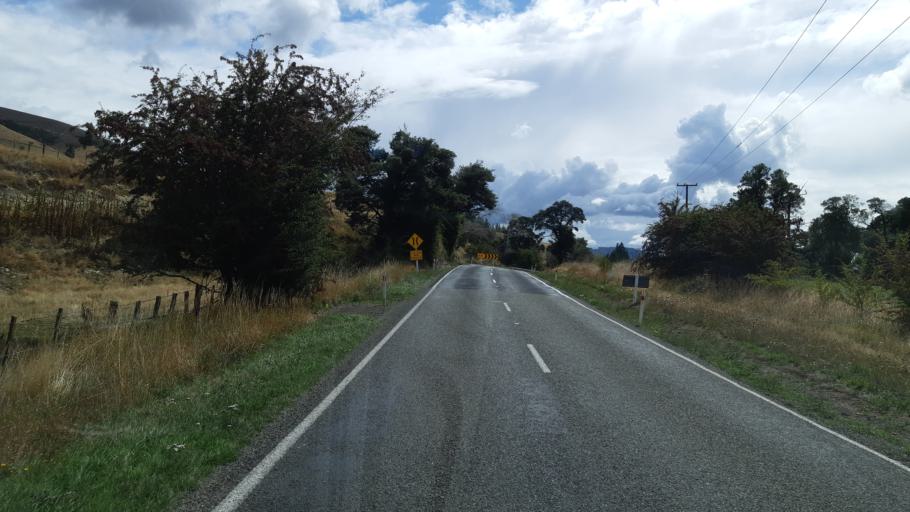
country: NZ
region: Tasman
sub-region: Tasman District
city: Wakefield
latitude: -41.5081
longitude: 172.7950
